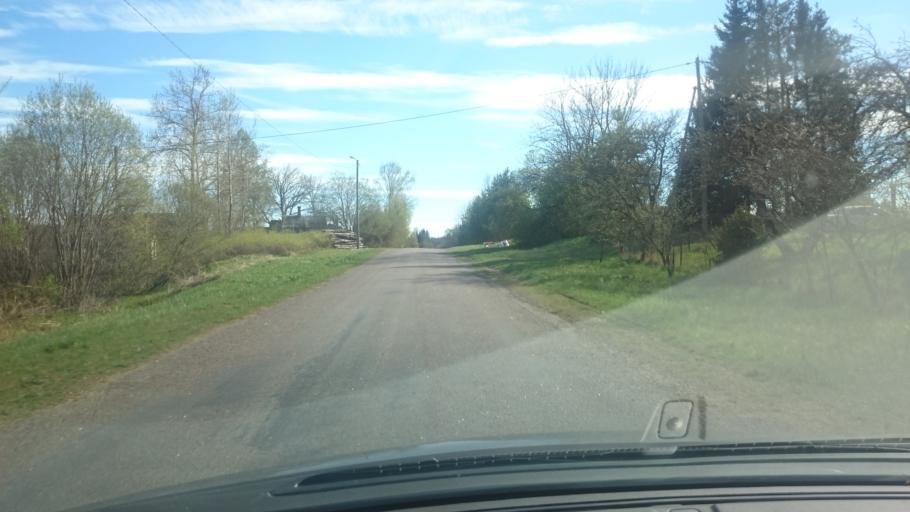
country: EE
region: Ida-Virumaa
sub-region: Sillamaee linn
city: Sillamae
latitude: 59.0874
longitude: 27.7820
